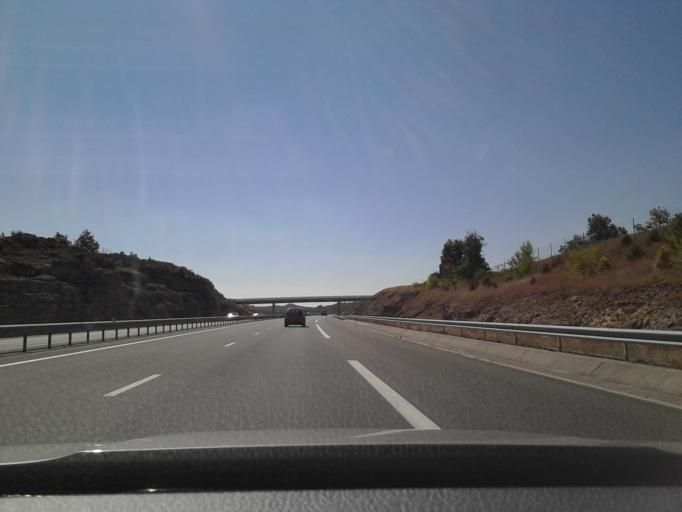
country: FR
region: Midi-Pyrenees
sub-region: Departement de l'Aveyron
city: Creissels
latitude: 44.0539
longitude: 3.0439
